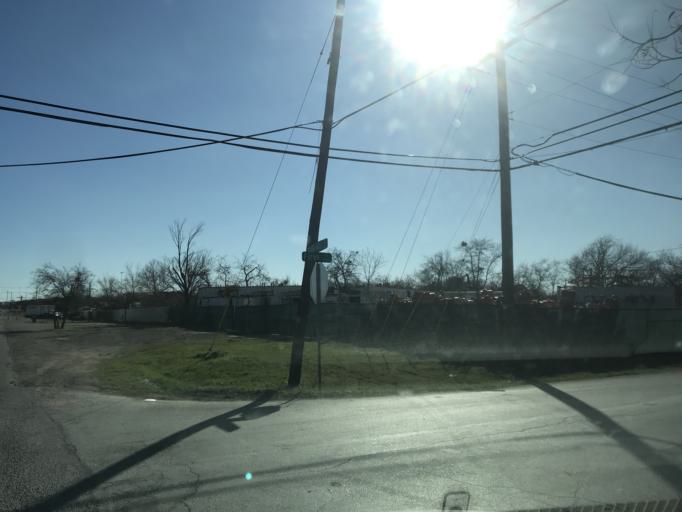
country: US
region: Texas
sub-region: Dallas County
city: Cockrell Hill
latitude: 32.7736
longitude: -96.9041
